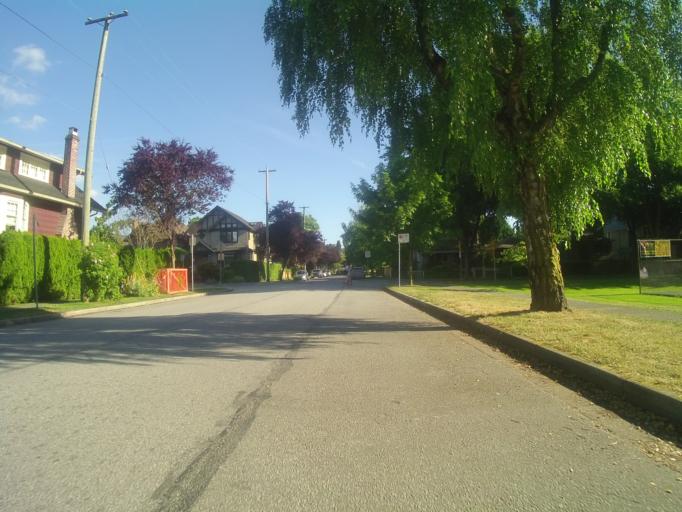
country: CA
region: British Columbia
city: Vancouver
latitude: 49.2546
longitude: -123.1202
